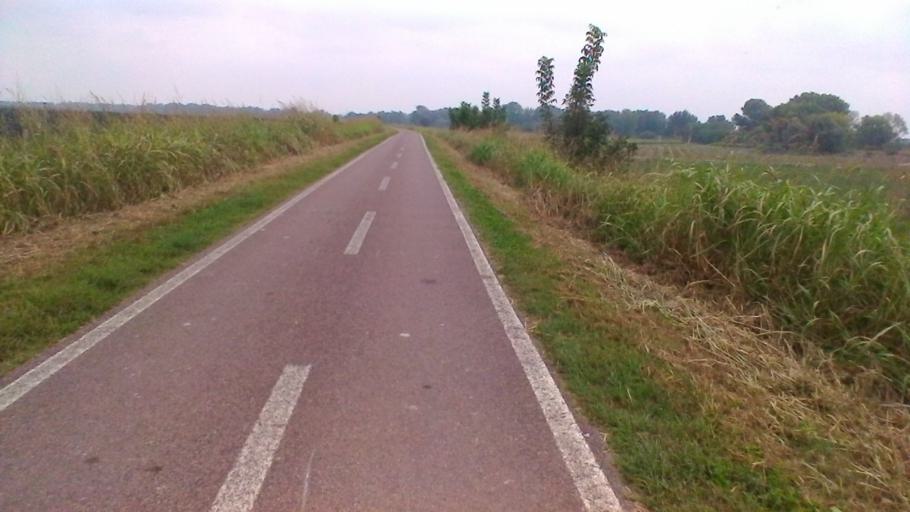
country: IT
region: Veneto
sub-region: Provincia di Verona
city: Zevio
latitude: 45.3837
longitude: 11.1061
